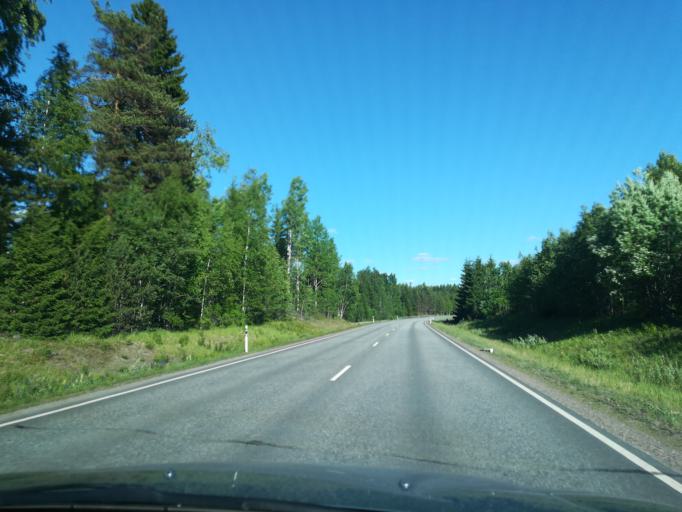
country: FI
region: South Karelia
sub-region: Imatra
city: Ruokolahti
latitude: 61.3498
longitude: 28.7545
